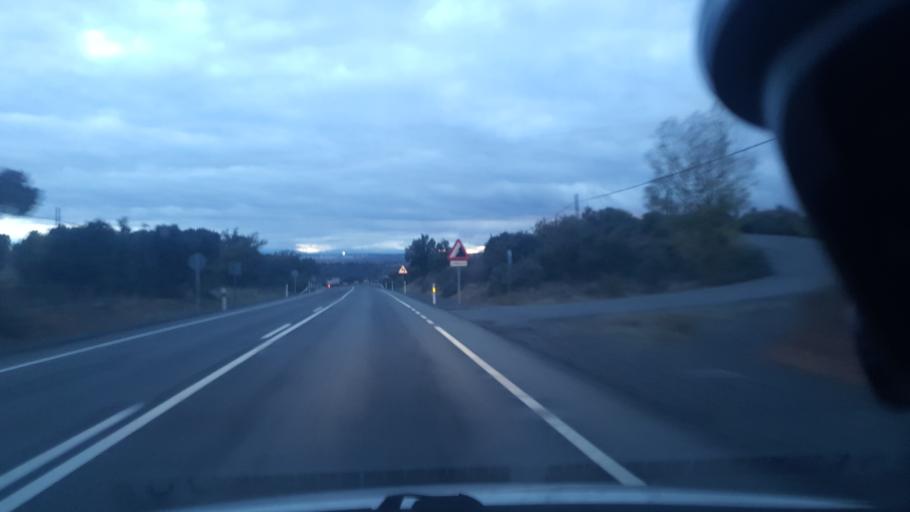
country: ES
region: Castille and Leon
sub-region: Provincia de Avila
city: Ojos-Albos
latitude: 40.7231
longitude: -4.5249
